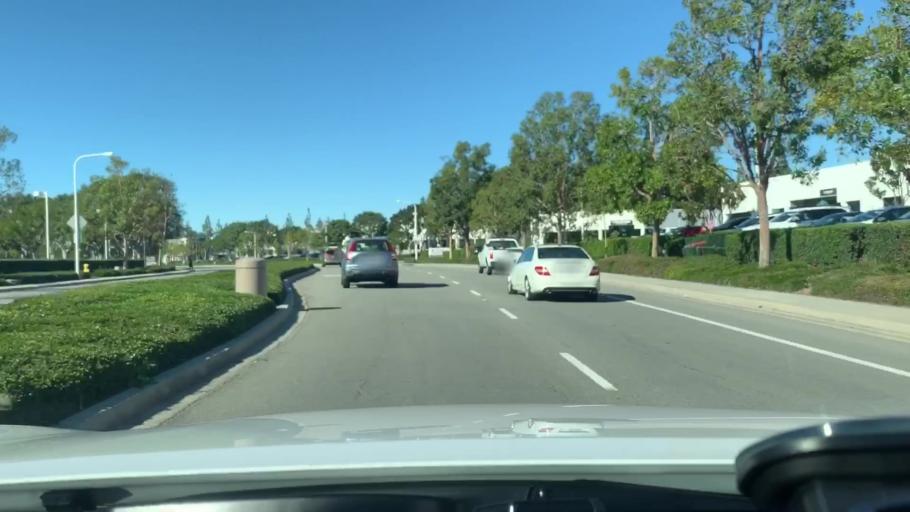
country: US
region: California
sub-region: Orange County
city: Laguna Woods
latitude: 33.6626
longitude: -117.7438
